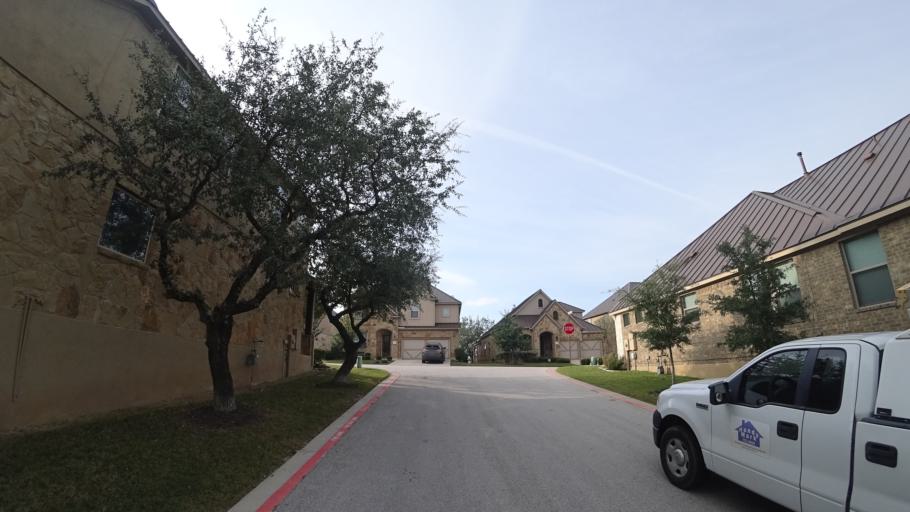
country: US
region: Texas
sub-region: Travis County
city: Hudson Bend
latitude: 30.3787
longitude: -97.8771
